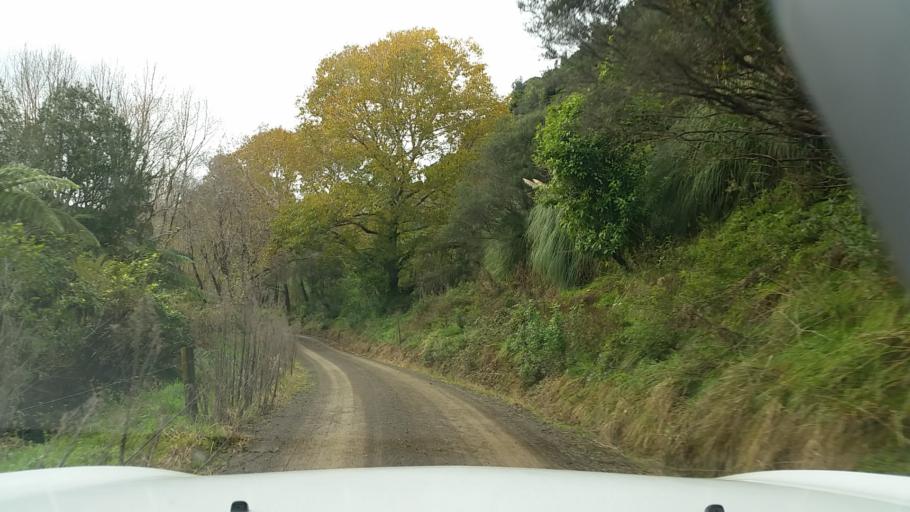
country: NZ
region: Taranaki
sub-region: New Plymouth District
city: Waitara
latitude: -38.7589
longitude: 174.6815
